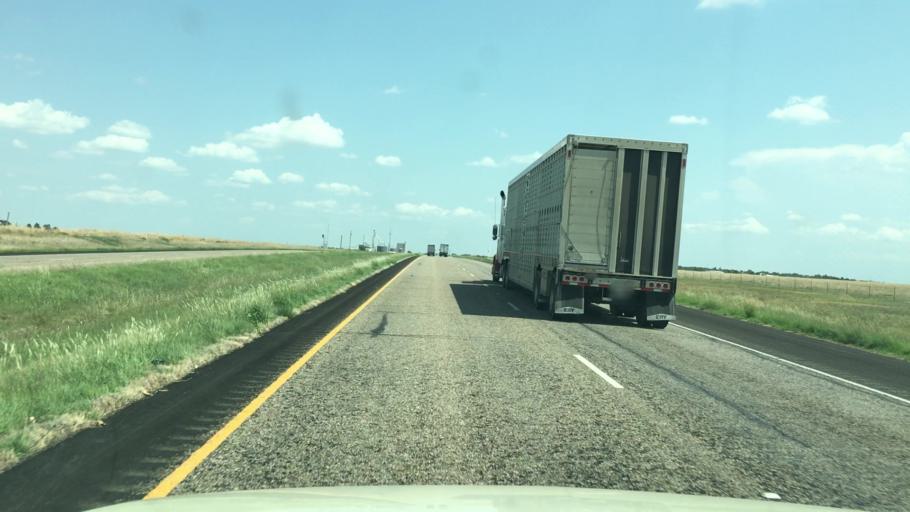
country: US
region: Texas
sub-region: Armstrong County
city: Claude
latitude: 35.1241
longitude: -101.3938
